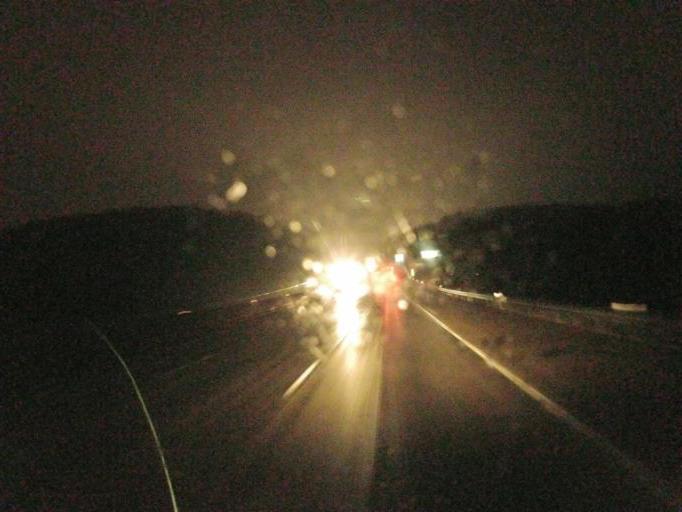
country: US
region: Missouri
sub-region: Franklin County
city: Pacific
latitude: 38.4907
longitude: -90.7416
